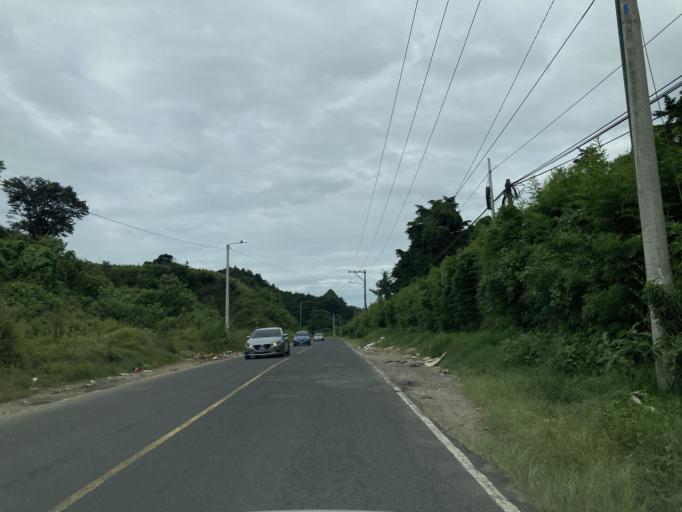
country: GT
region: Guatemala
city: San Jose Pinula
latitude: 14.5294
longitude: -90.4103
